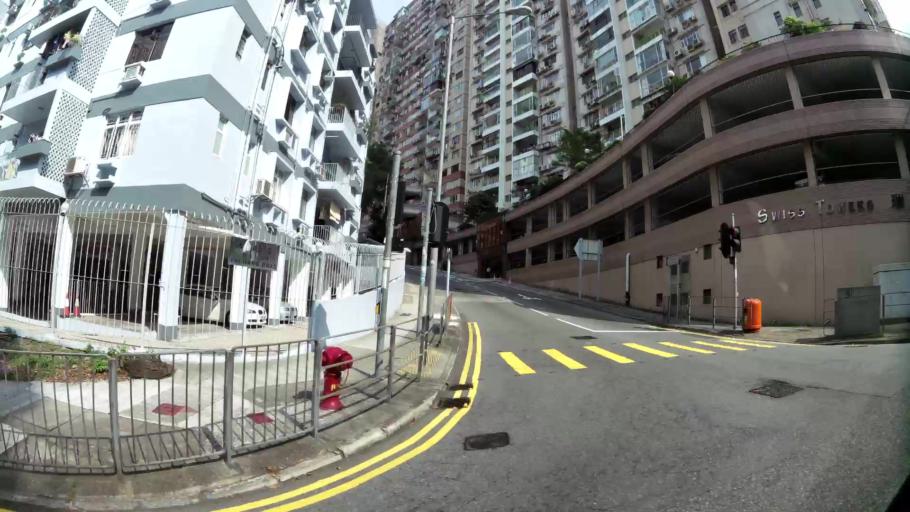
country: HK
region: Wanchai
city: Wan Chai
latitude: 22.2737
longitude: 114.1923
